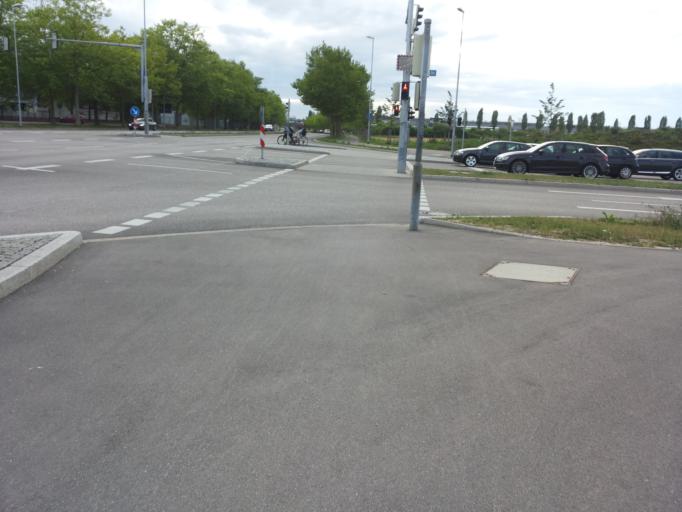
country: DE
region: Bavaria
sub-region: Upper Bavaria
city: Ingolstadt
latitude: 48.7736
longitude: 11.3970
